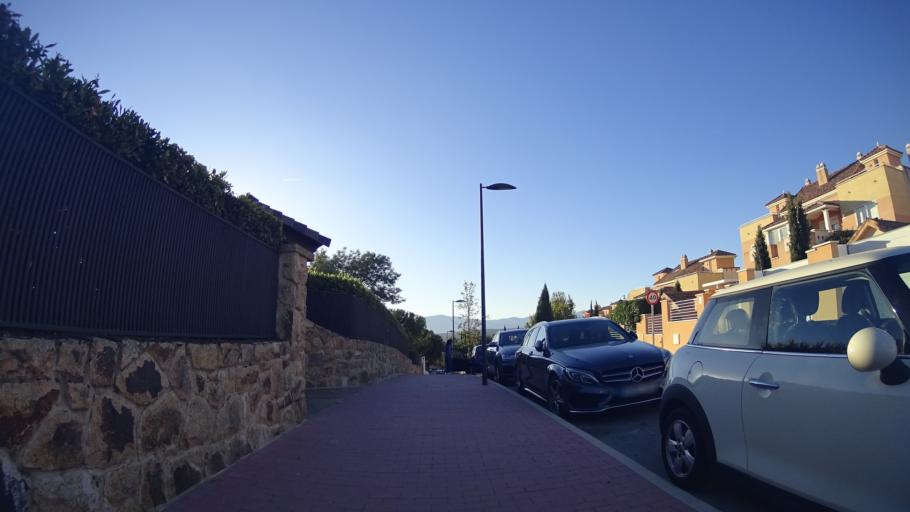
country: ES
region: Madrid
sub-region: Provincia de Madrid
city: Torrelodones
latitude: 40.5752
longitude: -3.9401
